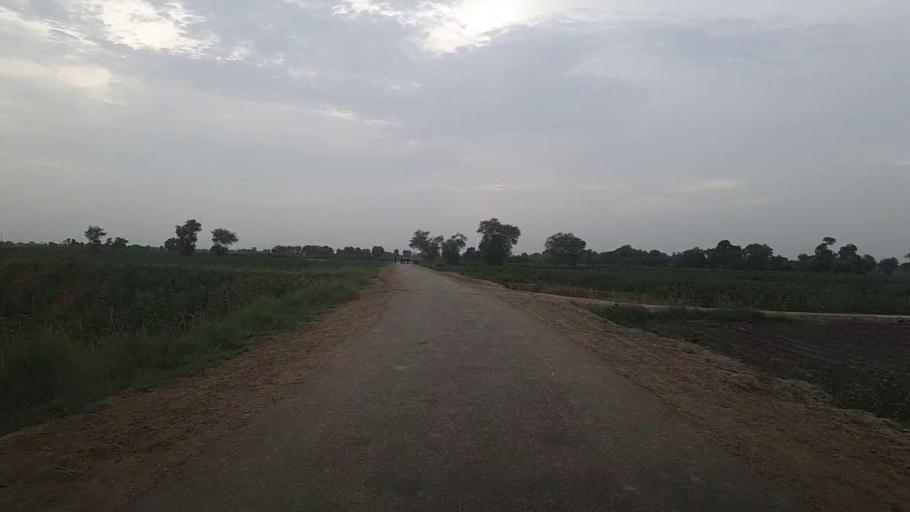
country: PK
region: Sindh
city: Karaundi
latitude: 26.9572
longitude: 68.3615
